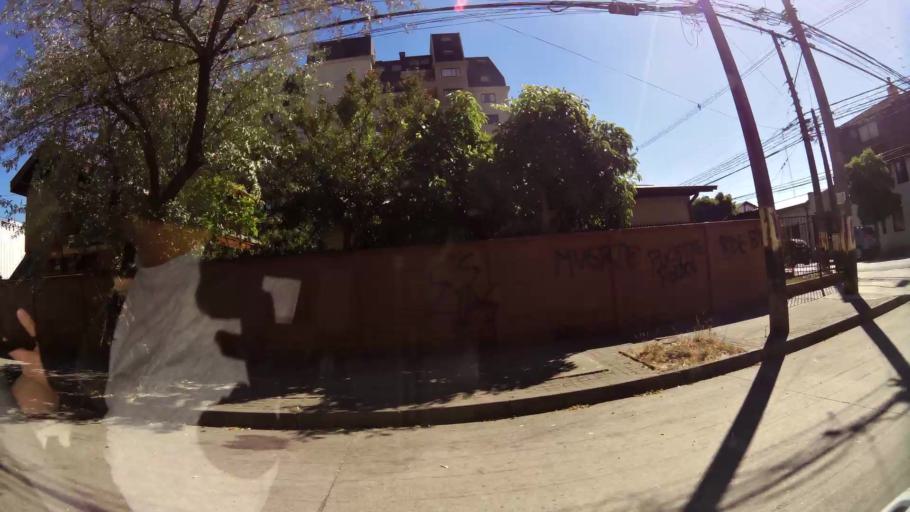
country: CL
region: Biobio
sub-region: Provincia de Concepcion
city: Concepcion
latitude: -36.8171
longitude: -73.0398
